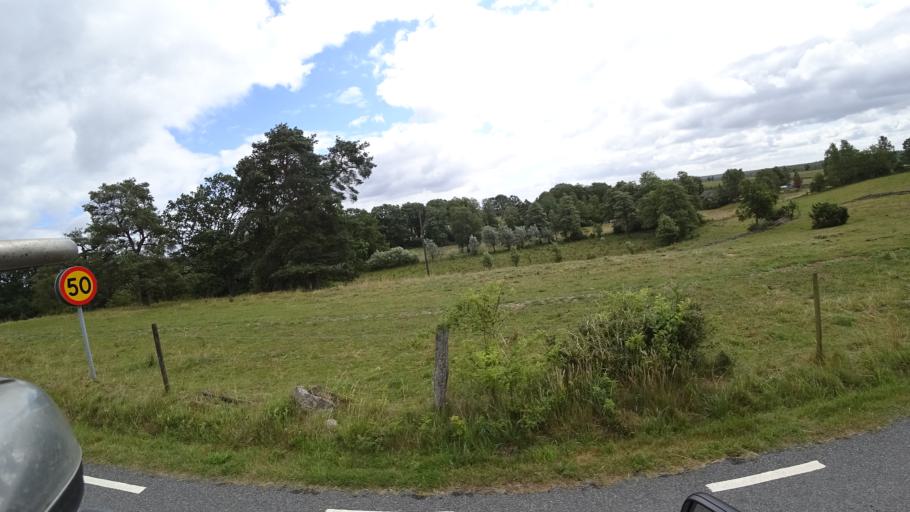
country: SE
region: Skane
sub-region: Kristianstads Kommun
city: Degeberga
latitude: 55.7296
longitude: 14.0003
